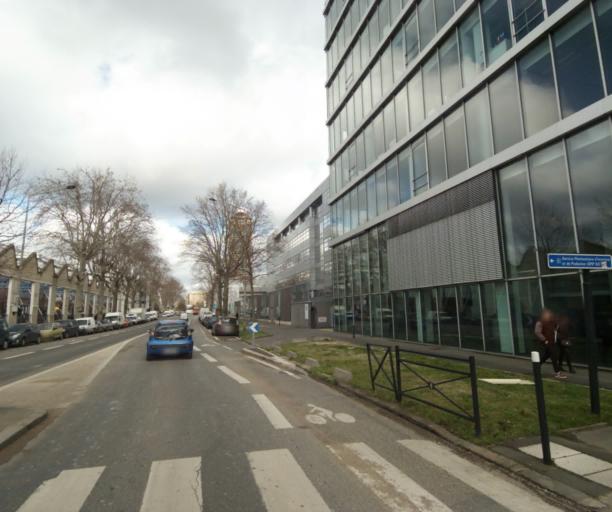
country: FR
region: Ile-de-France
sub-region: Paris
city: Saint-Ouen
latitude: 48.9157
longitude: 2.3443
